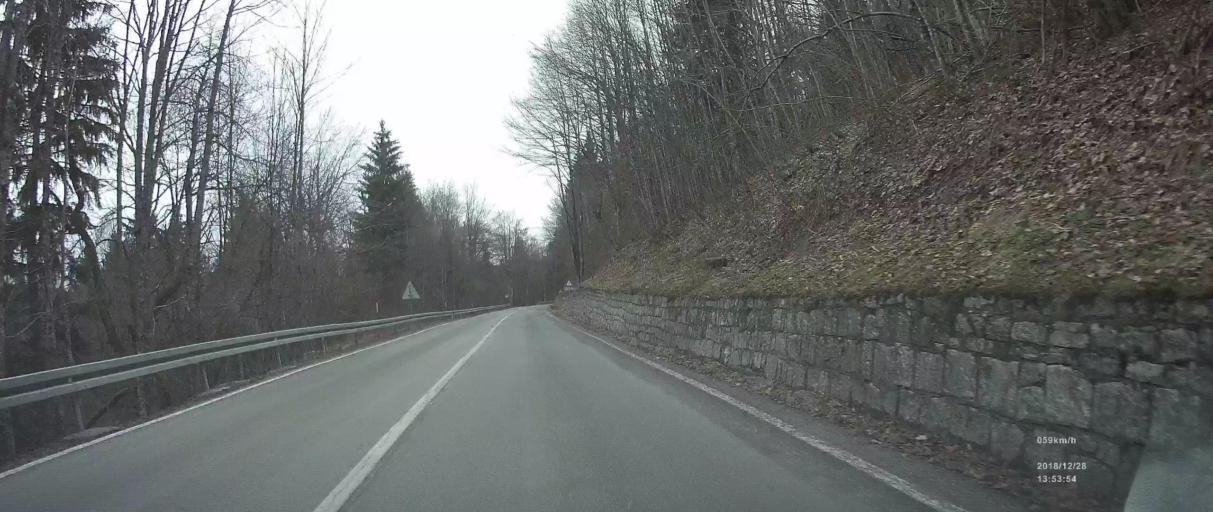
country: HR
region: Primorsko-Goranska
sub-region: Grad Delnice
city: Delnice
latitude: 45.3890
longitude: 14.8569
